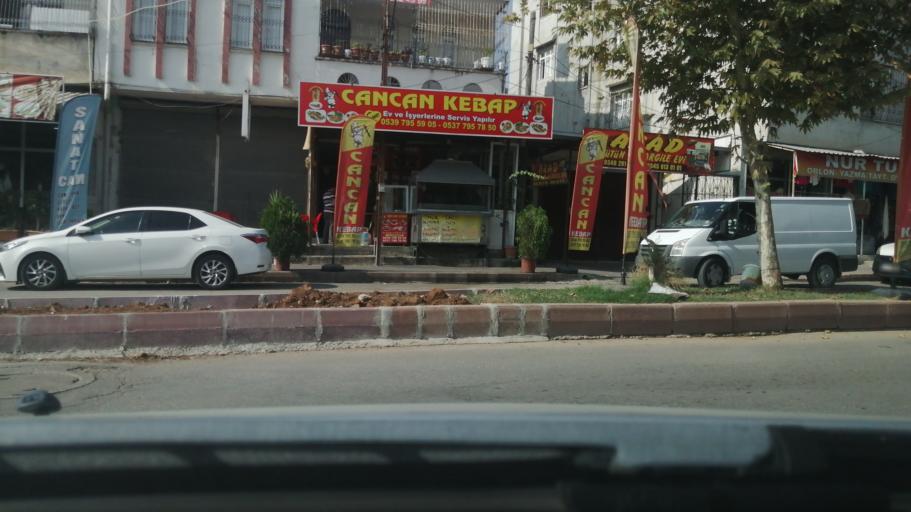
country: TR
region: Adana
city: Seyhan
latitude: 37.0181
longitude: 35.2732
